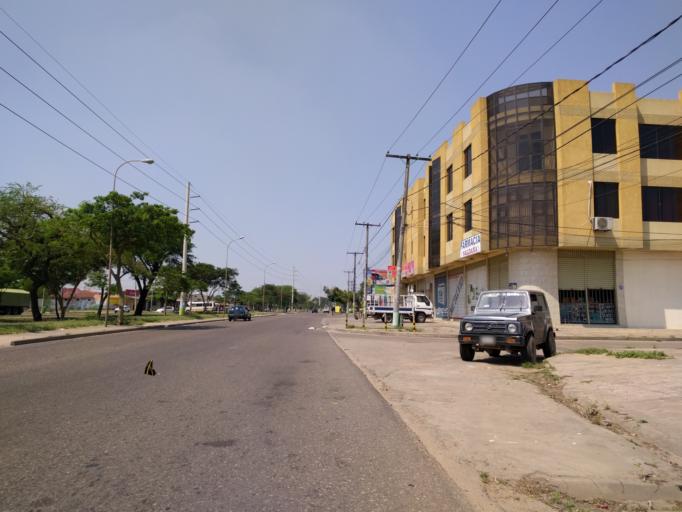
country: BO
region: Santa Cruz
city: Santa Cruz de la Sierra
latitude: -17.7925
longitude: -63.1487
